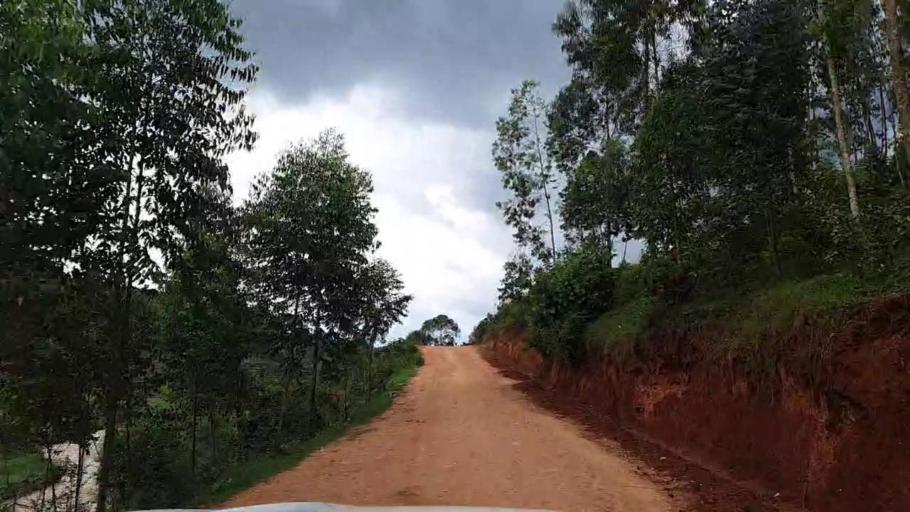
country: RW
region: Southern Province
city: Nyanza
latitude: -2.3922
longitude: 29.6842
